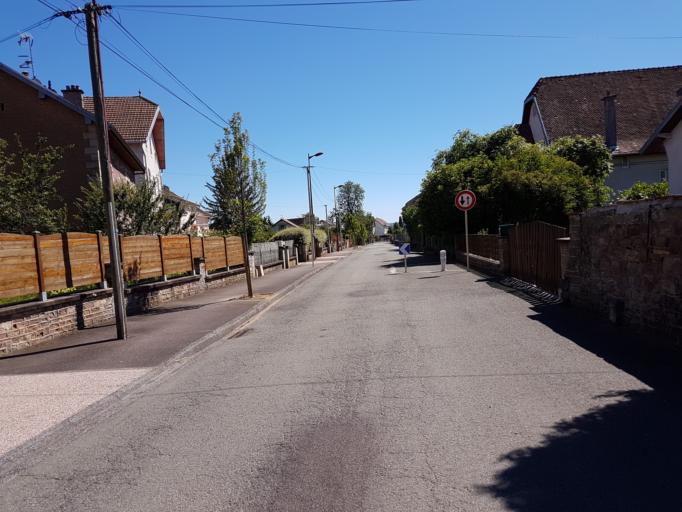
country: FR
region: Franche-Comte
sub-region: Departement de la Haute-Saone
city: Saint-Sauveur
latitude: 47.8133
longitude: 6.3855
